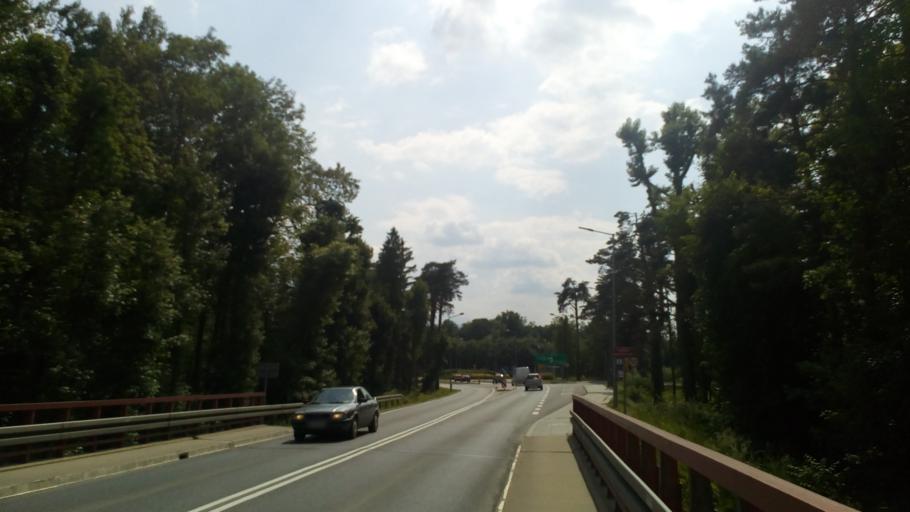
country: PL
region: Lesser Poland Voivodeship
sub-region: Powiat nowosadecki
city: Stary Sacz
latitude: 49.5687
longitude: 20.6585
